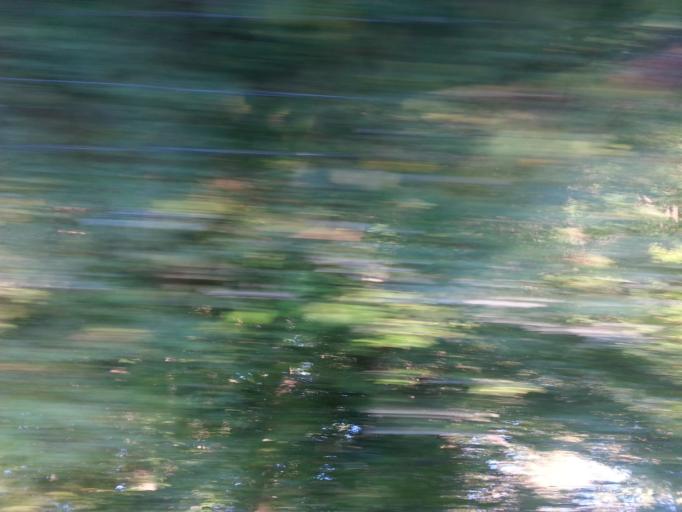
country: US
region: Tennessee
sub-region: Blount County
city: Wildwood
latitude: 35.8837
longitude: -83.8738
